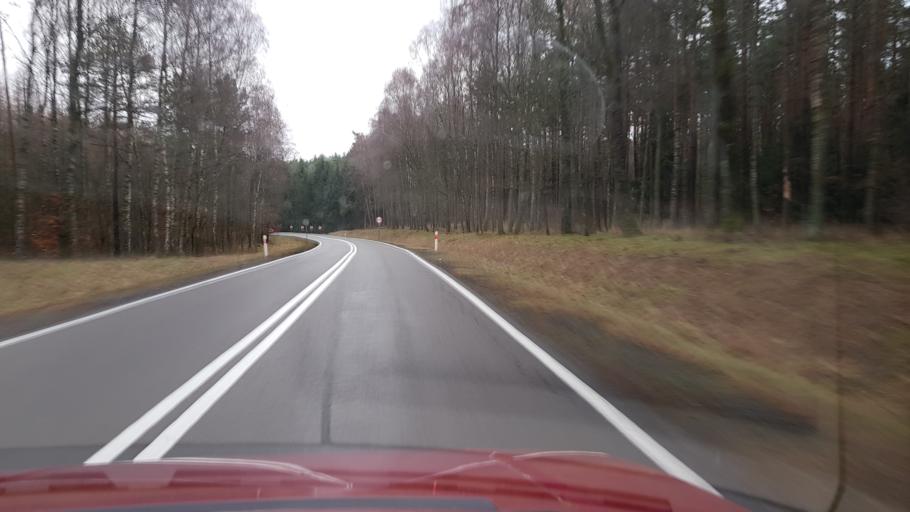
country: PL
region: West Pomeranian Voivodeship
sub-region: Powiat drawski
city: Drawsko Pomorskie
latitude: 53.4922
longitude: 15.7070
